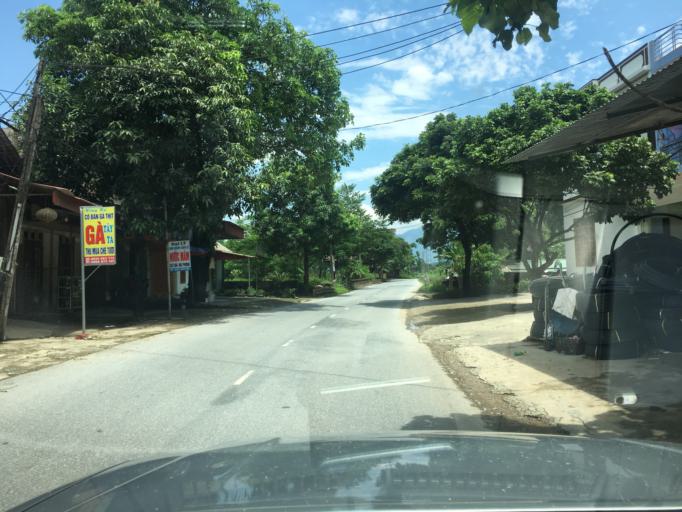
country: VN
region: Yen Bai
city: Son Thinh
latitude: 21.6481
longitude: 104.5008
